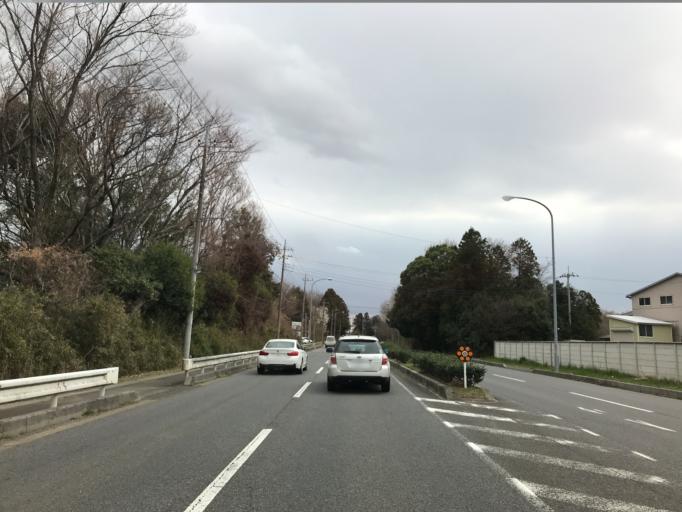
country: JP
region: Ibaraki
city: Ushiku
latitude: 36.0124
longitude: 140.0835
